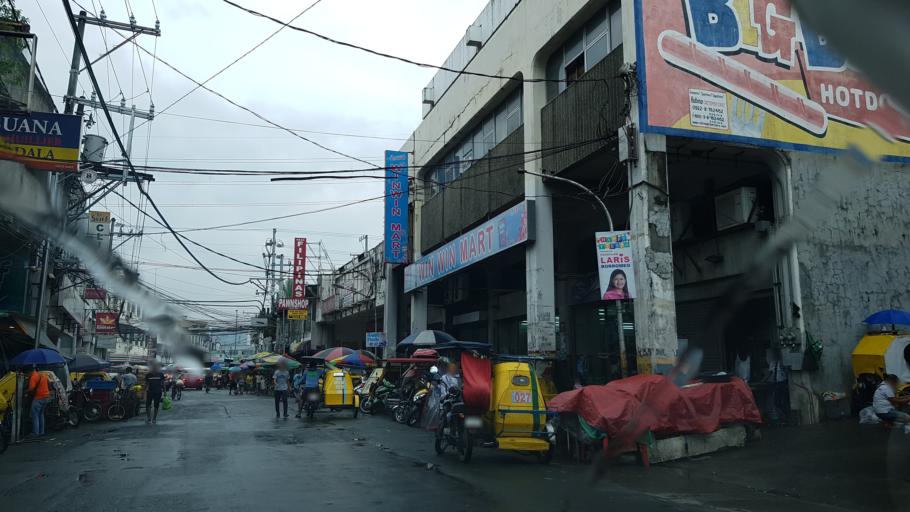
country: PH
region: Metro Manila
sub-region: City of Manila
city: Quiapo
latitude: 14.5774
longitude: 120.9935
